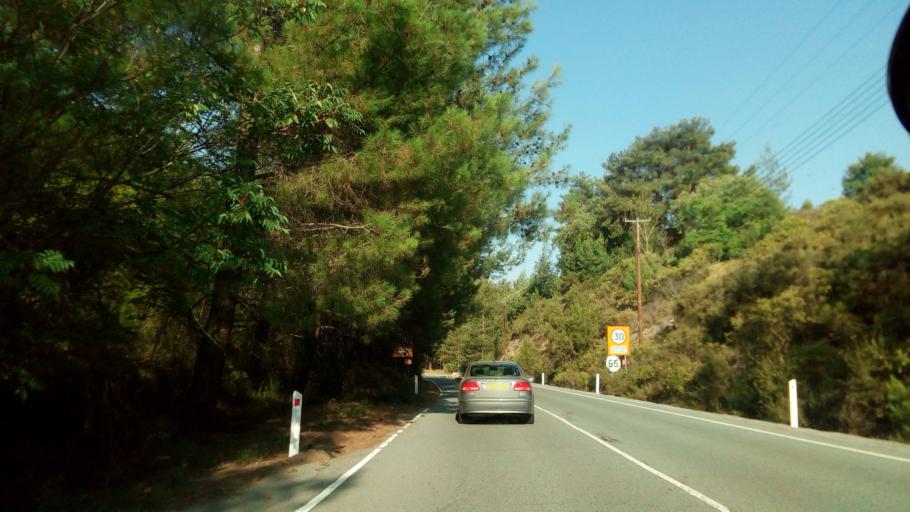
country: CY
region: Limassol
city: Pelendri
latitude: 34.8644
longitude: 32.8628
